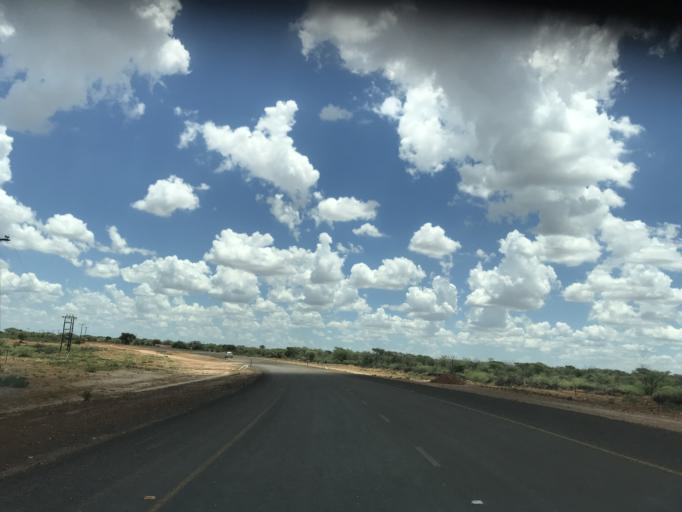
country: BW
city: Mabuli
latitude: -25.8011
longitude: 24.7099
